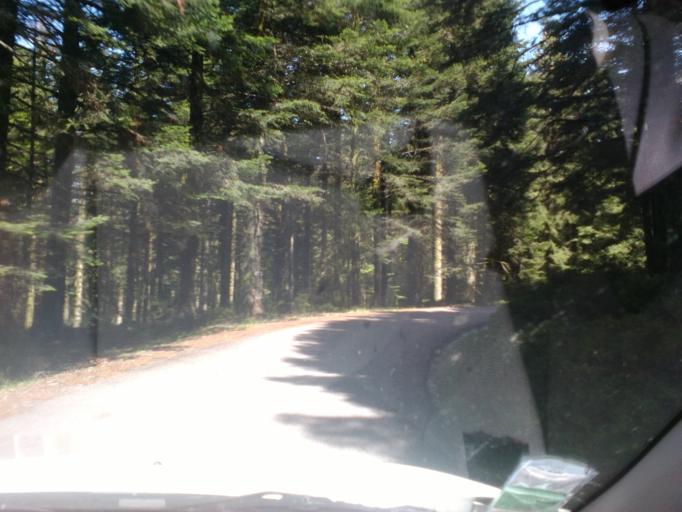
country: FR
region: Lorraine
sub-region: Departement des Vosges
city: Le Tholy
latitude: 48.0523
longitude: 6.7723
